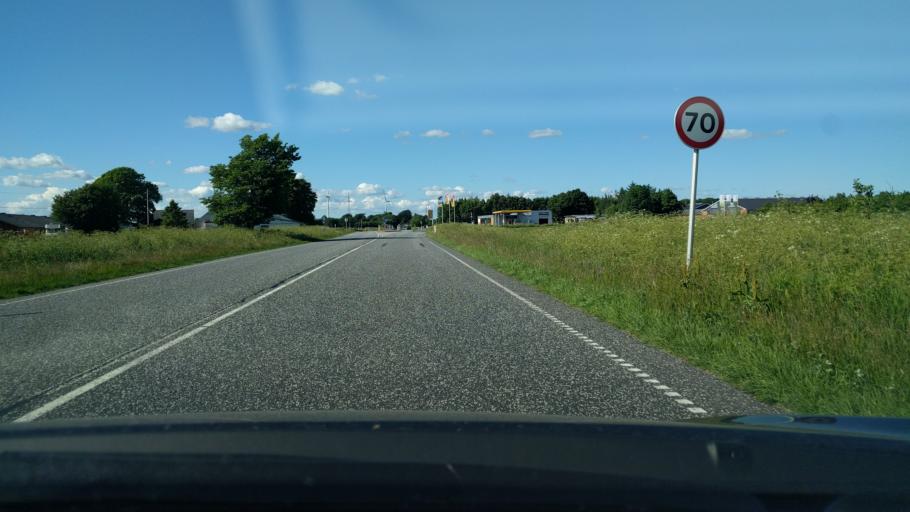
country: DK
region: North Denmark
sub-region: Vesthimmerland Kommune
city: Alestrup
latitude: 56.6632
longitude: 9.5217
